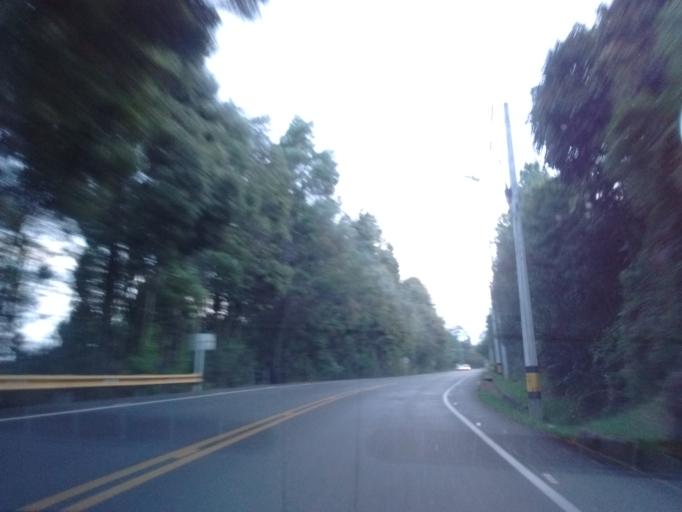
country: CO
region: Antioquia
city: Envigado
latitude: 6.1631
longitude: -75.5027
